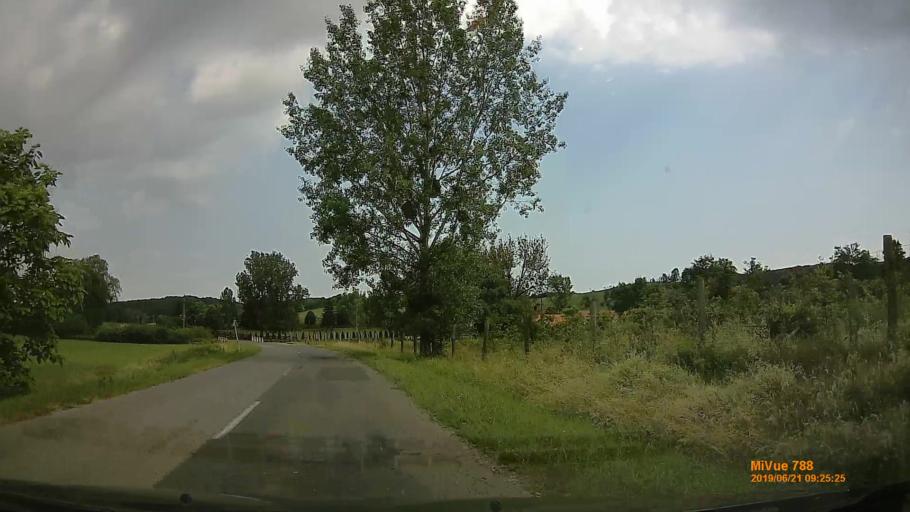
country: HU
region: Somogy
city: Taszar
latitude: 46.2651
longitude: 17.9079
